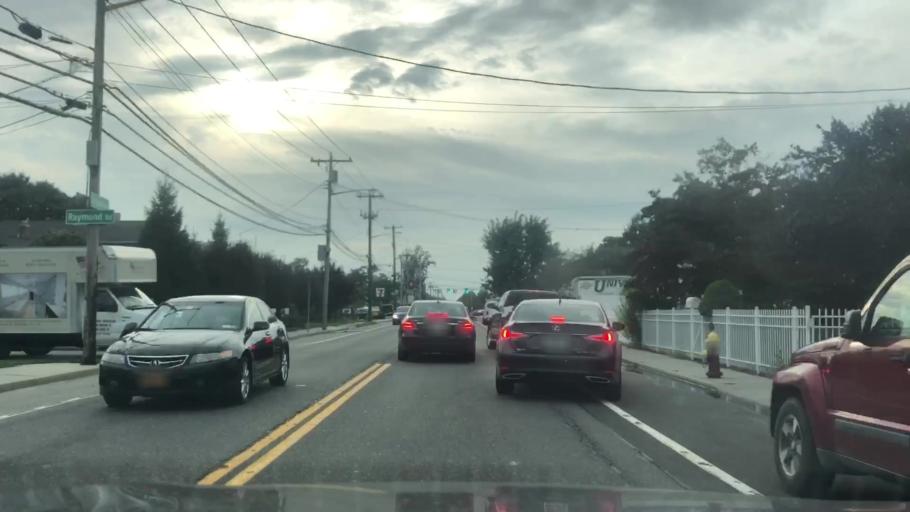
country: US
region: New York
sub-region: Nassau County
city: North Bellmore
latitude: 40.6916
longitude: -73.5314
